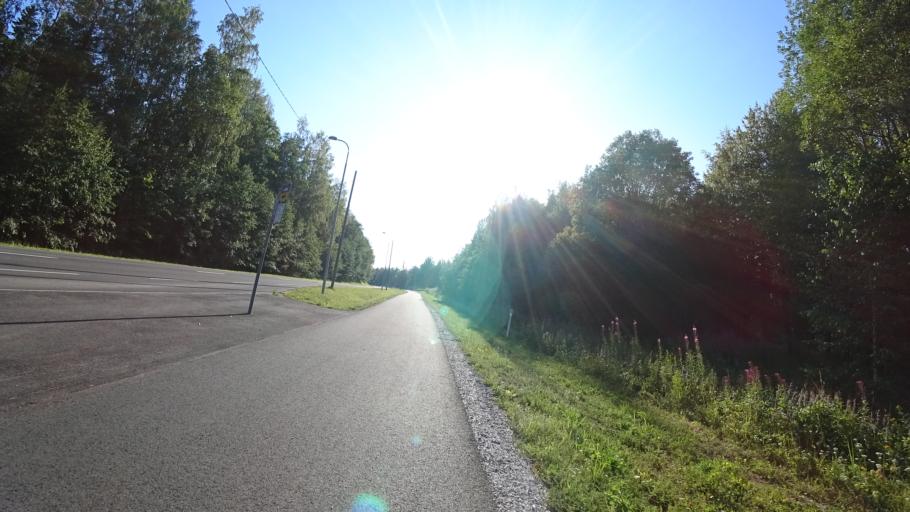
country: FI
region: Pirkanmaa
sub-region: Tampere
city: Pirkkala
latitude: 61.4927
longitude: 23.6010
